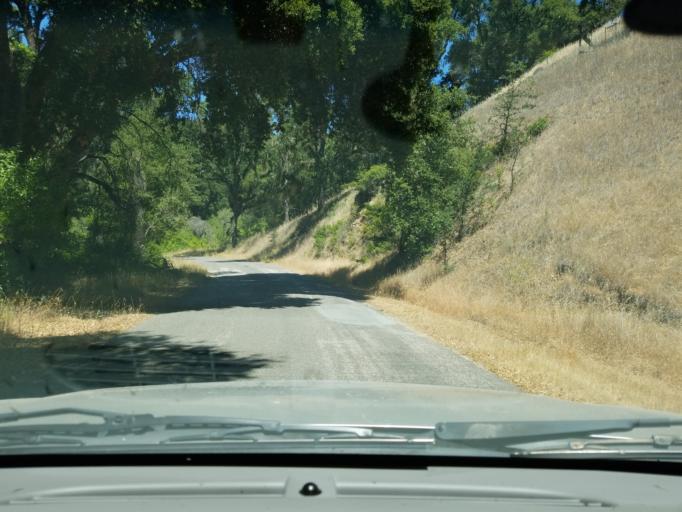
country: US
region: California
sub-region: Monterey County
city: Gonzales
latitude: 36.3530
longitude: -121.5432
